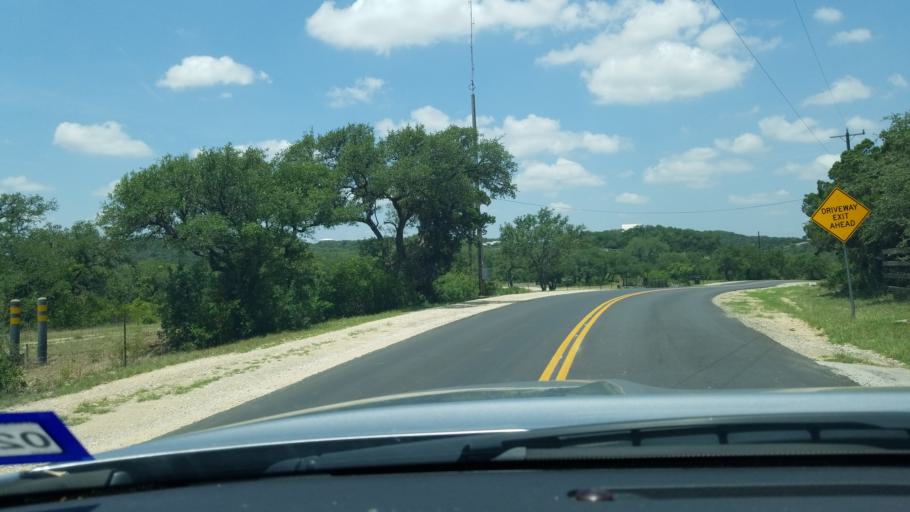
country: US
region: Texas
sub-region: Bexar County
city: Timberwood Park
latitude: 29.7027
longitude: -98.4554
